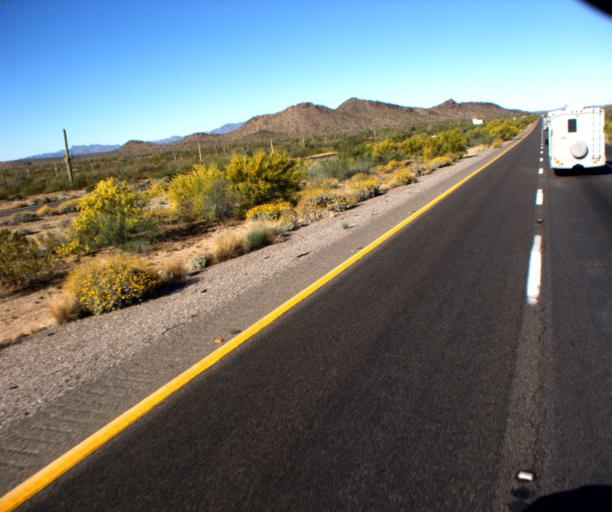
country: US
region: Arizona
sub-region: Pinal County
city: Maricopa
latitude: 32.8353
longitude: -112.1637
